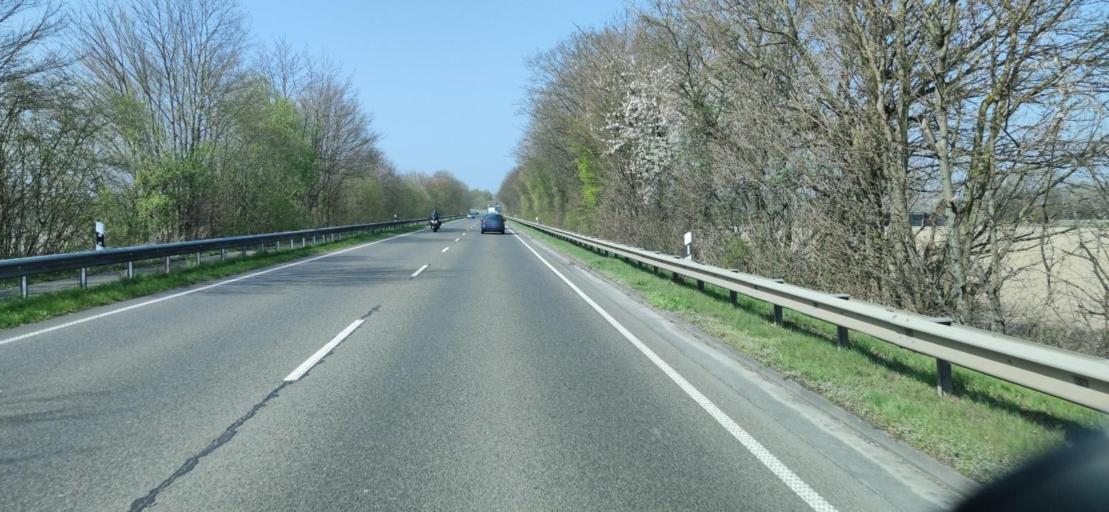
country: DE
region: North Rhine-Westphalia
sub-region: Regierungsbezirk Dusseldorf
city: Korschenbroich
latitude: 51.2200
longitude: 6.5039
